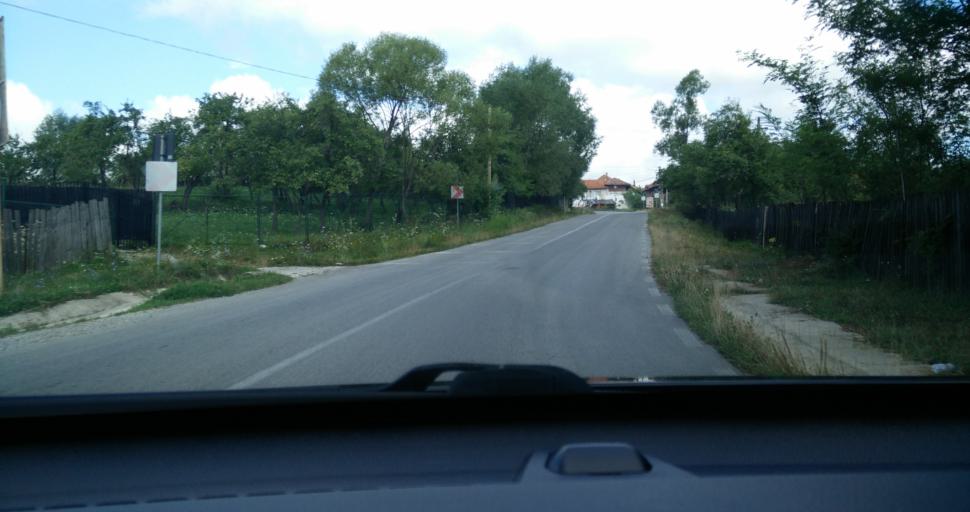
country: RO
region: Gorj
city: Novaci-Straini
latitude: 45.1762
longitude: 23.7062
